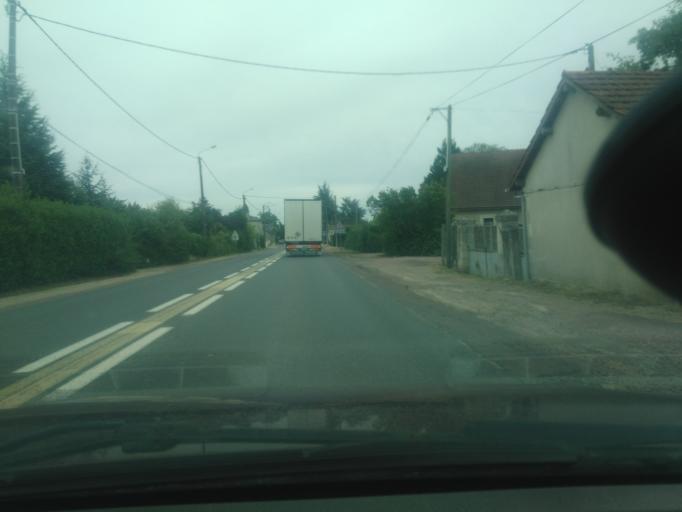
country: FR
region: Poitou-Charentes
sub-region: Departement de la Vienne
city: Sevres-Anxaumont
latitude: 46.5607
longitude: 0.4416
